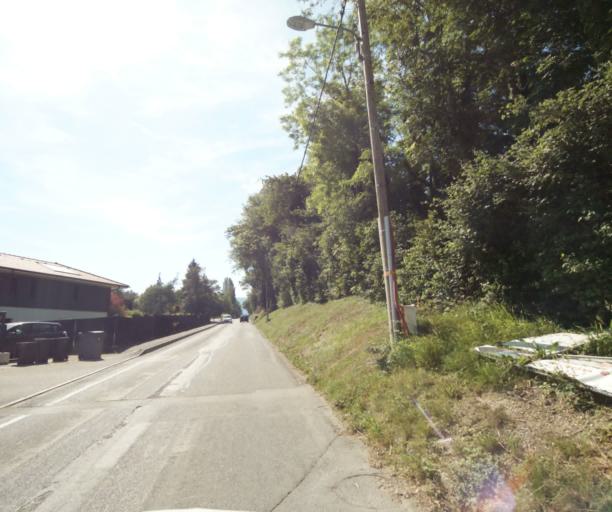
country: FR
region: Rhone-Alpes
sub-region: Departement de la Haute-Savoie
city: Anthy-sur-Leman
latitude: 46.3556
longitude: 6.4332
